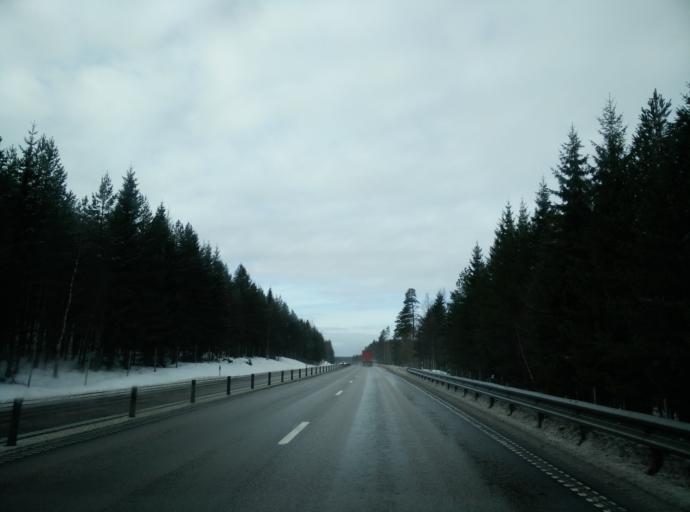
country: SE
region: Dalarna
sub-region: Hedemora Kommun
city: Langshyttan
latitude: 60.5564
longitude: 16.0626
